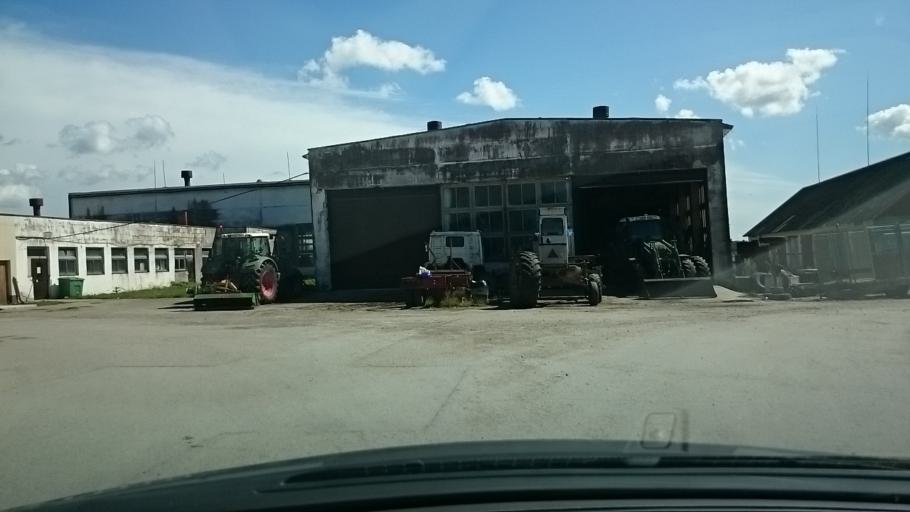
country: EE
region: Laeaene
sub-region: Haapsalu linn
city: Haapsalu
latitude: 59.0056
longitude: 23.5234
